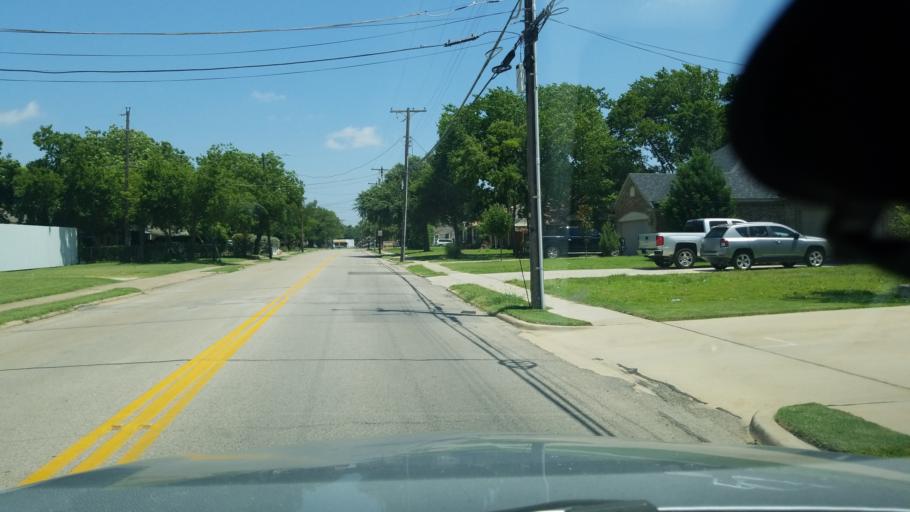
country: US
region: Texas
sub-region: Dallas County
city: Irving
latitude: 32.8192
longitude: -96.9635
